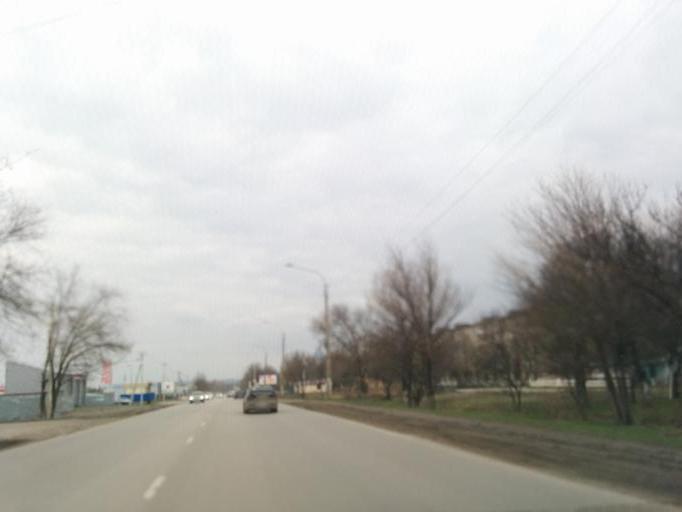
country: RU
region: Rostov
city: Krasyukovskaya
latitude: 47.4879
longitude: 40.1029
